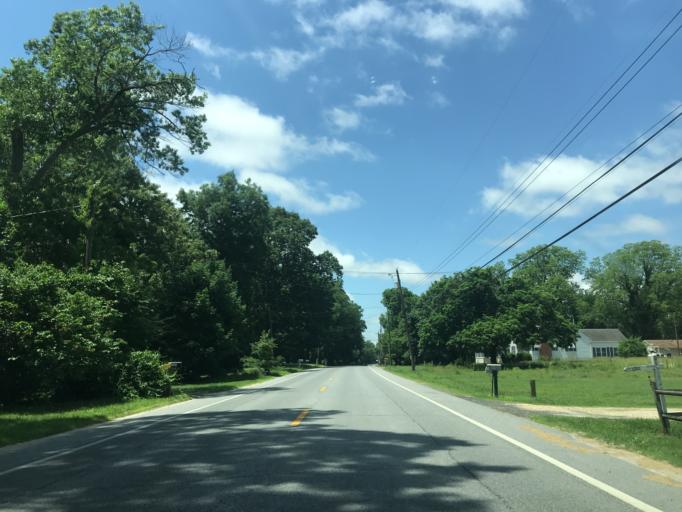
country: US
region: Maryland
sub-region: Caroline County
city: Federalsburg
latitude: 38.6945
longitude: -75.7519
